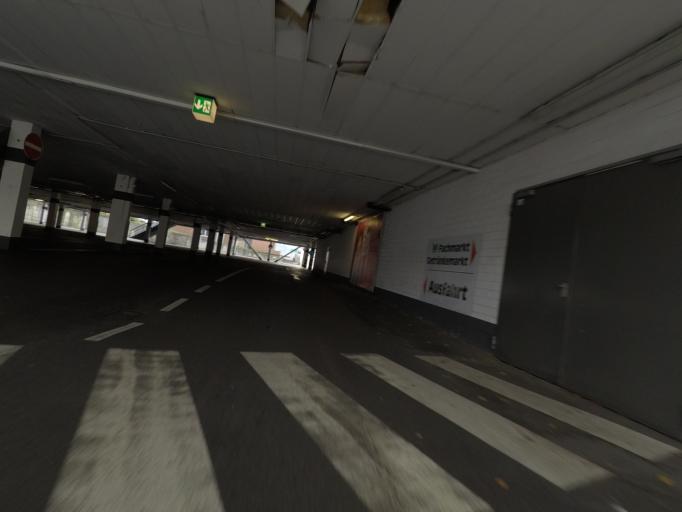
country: DE
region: Baden-Wuerttemberg
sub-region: Tuebingen Region
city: Pfullingen
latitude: 48.4798
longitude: 9.2218
